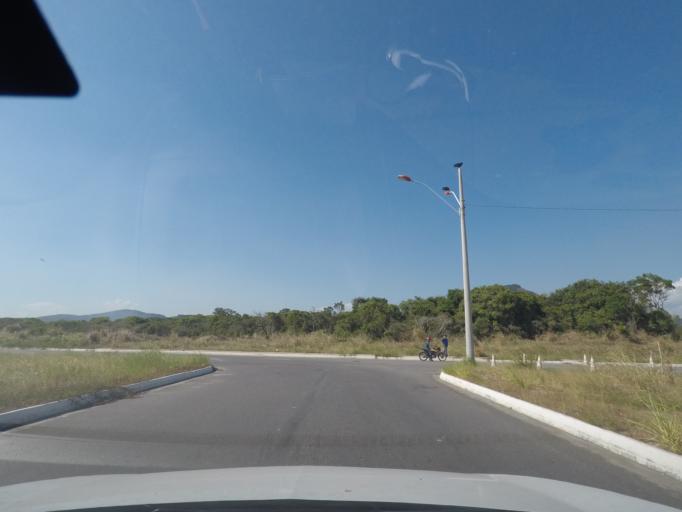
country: BR
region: Rio de Janeiro
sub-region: Marica
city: Marica
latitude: -22.9569
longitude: -42.9272
